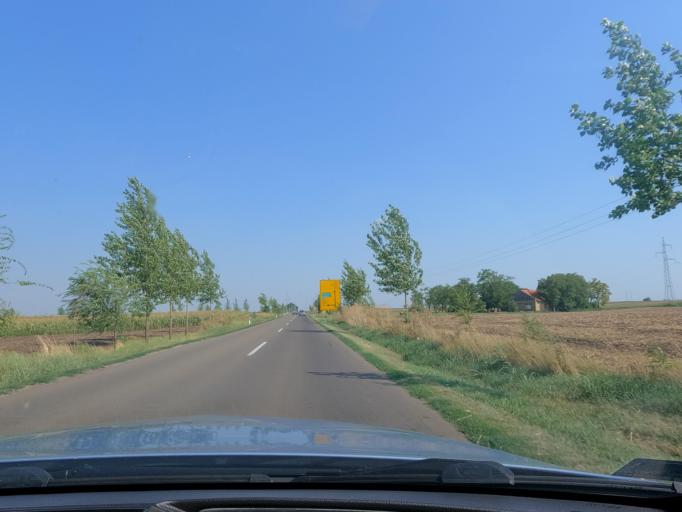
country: RS
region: Autonomna Pokrajina Vojvodina
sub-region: Severnobacki Okrug
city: Backa Topola
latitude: 45.8011
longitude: 19.6575
